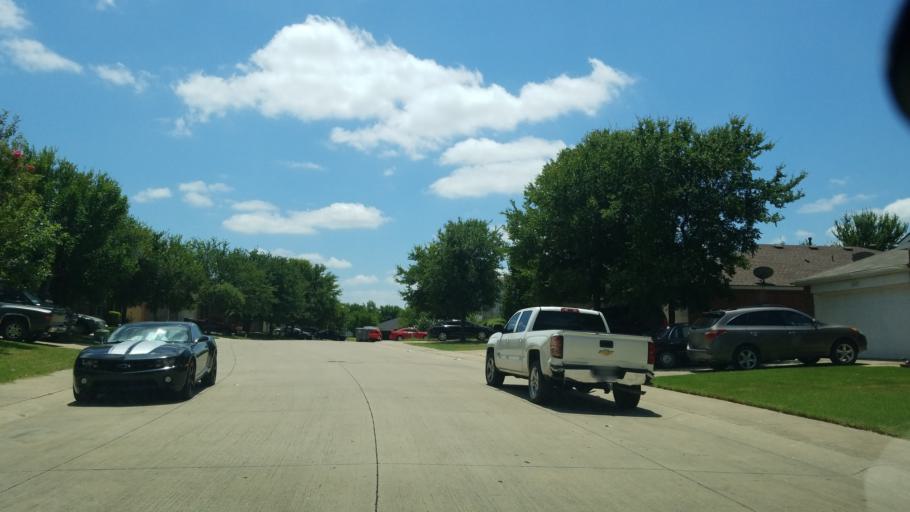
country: US
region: Texas
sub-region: Dallas County
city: Balch Springs
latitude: 32.7460
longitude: -96.7018
